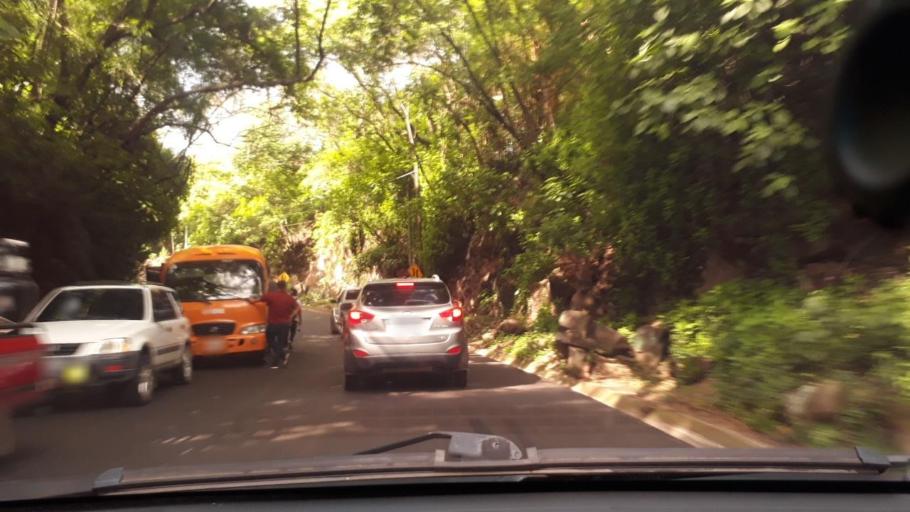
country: GT
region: Jutiapa
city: Quesada
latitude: 14.2713
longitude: -90.0044
